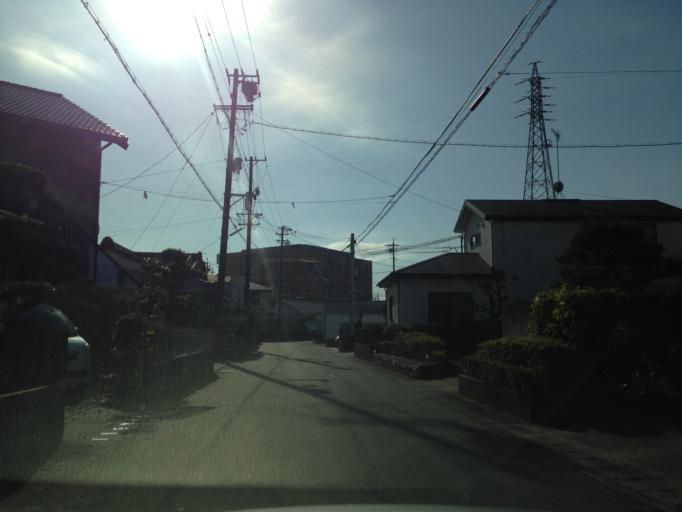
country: JP
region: Shizuoka
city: Fukuroi
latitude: 34.7506
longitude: 137.9265
